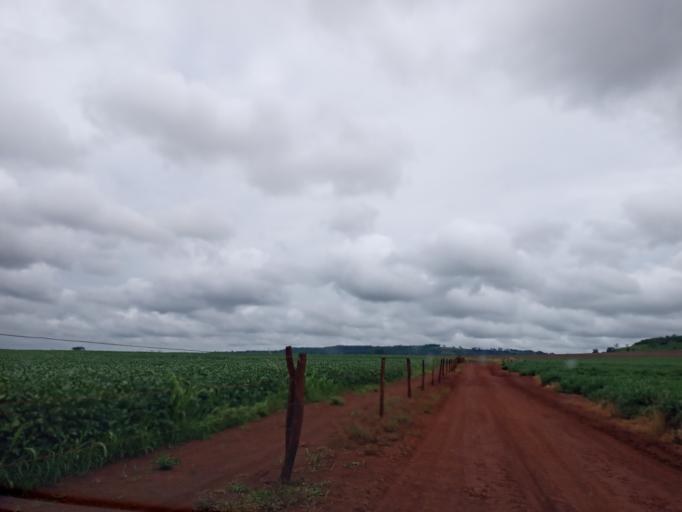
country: BR
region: Minas Gerais
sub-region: Centralina
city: Centralina
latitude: -18.5913
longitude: -49.1451
